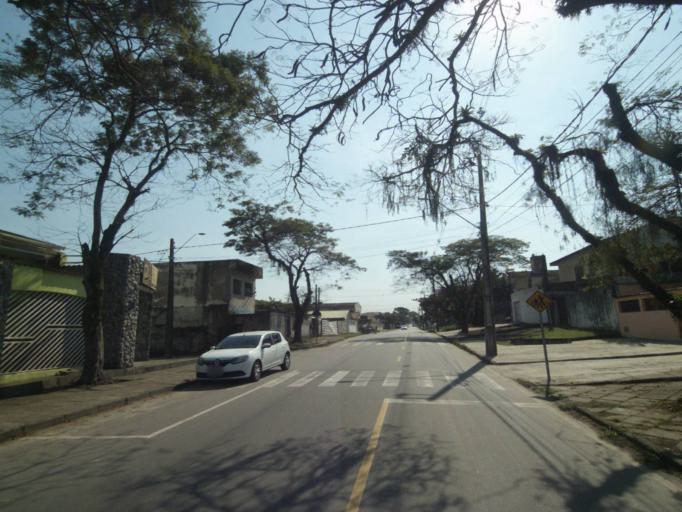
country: BR
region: Parana
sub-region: Paranagua
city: Paranagua
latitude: -25.5346
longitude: -48.5285
